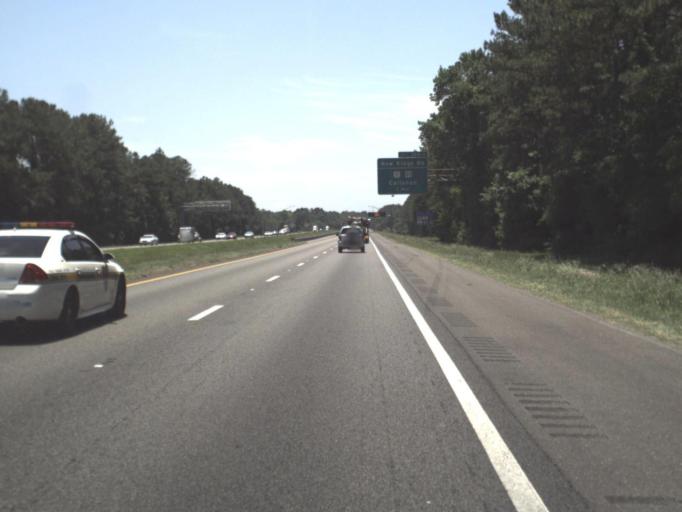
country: US
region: Florida
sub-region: Nassau County
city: Nassau Village-Ratliff
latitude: 30.4279
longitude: -81.7312
